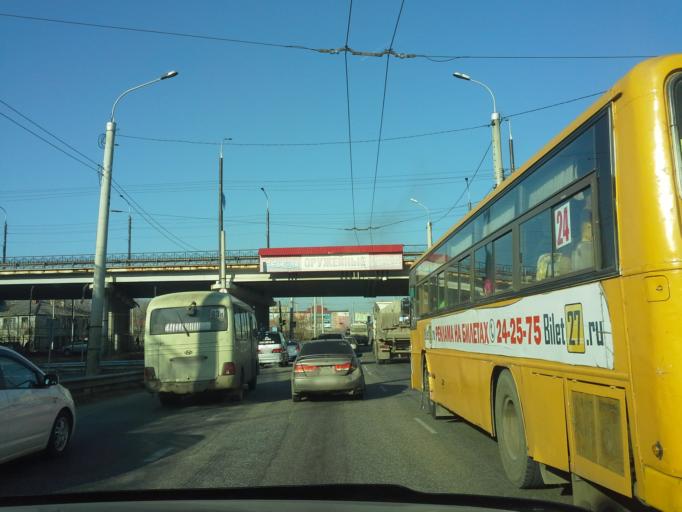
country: RU
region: Khabarovsk Krai
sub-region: Khabarovskiy Rayon
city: Khabarovsk
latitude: 48.4768
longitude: 135.1166
